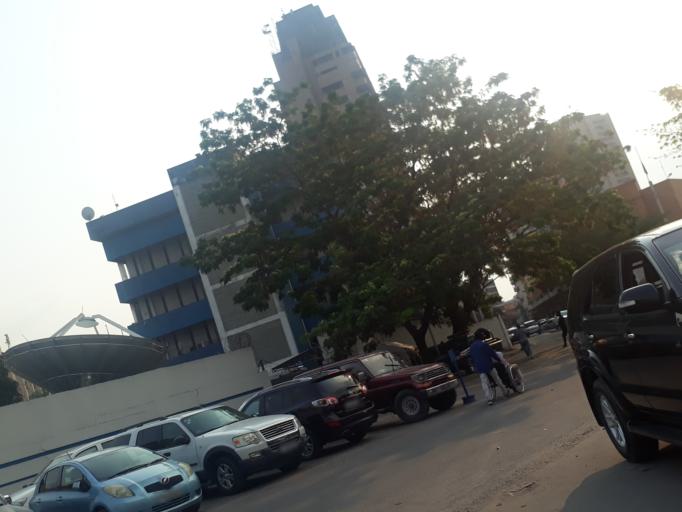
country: CD
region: Kinshasa
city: Kinshasa
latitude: -4.3013
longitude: 15.3157
